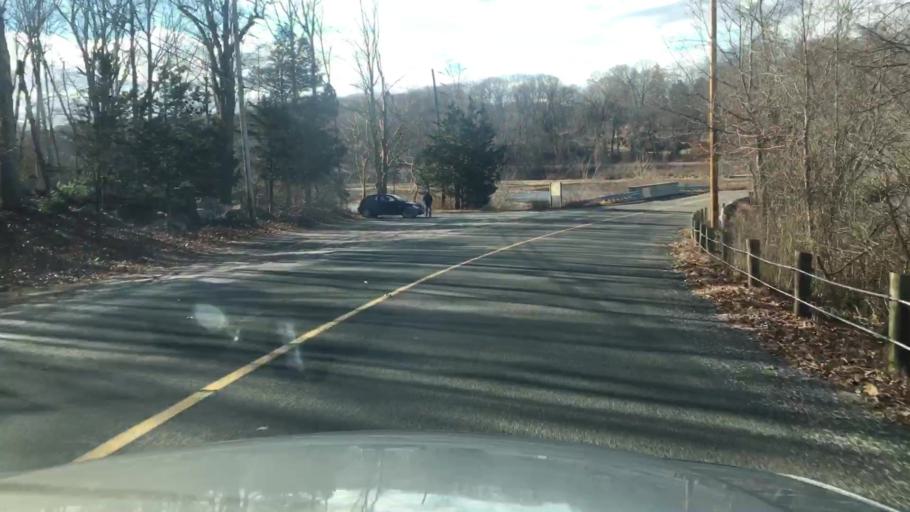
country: US
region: Connecticut
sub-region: Middlesex County
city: Deep River Center
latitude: 41.3832
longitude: -72.4253
